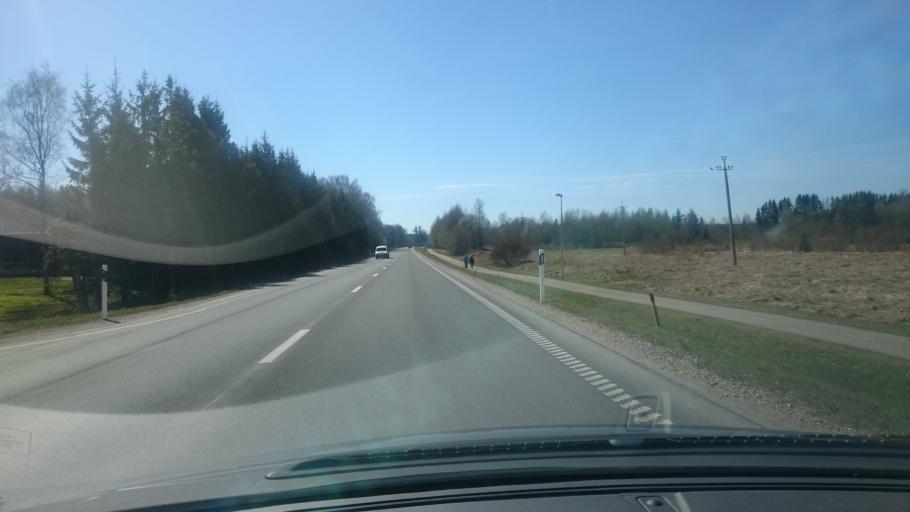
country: EE
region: Raplamaa
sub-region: Rapla vald
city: Rapla
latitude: 58.9841
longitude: 24.8427
